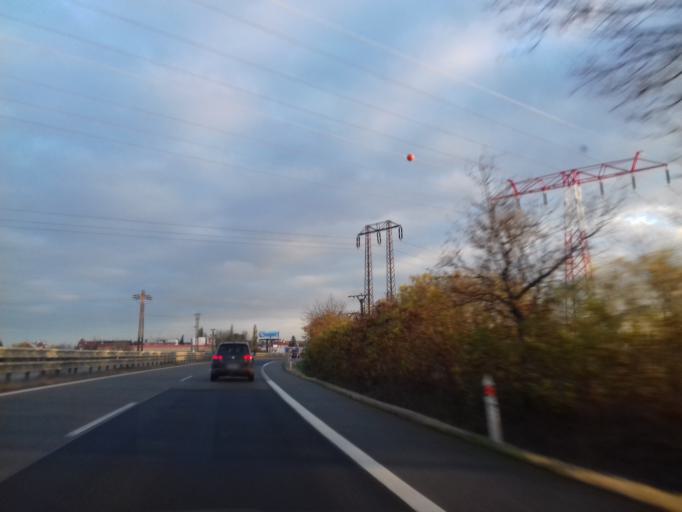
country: CZ
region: Olomoucky
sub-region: Okres Prostejov
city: Prostejov
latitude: 49.4596
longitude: 17.1175
